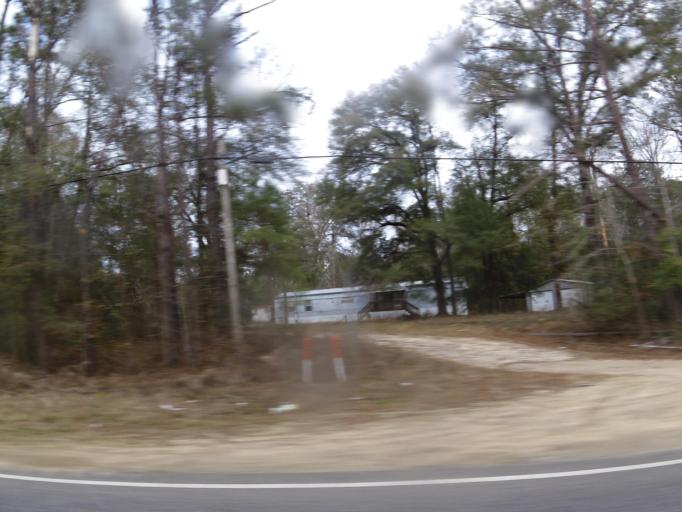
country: US
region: Alabama
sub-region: Barbour County
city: Eufaula
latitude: 31.9467
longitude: -85.1910
